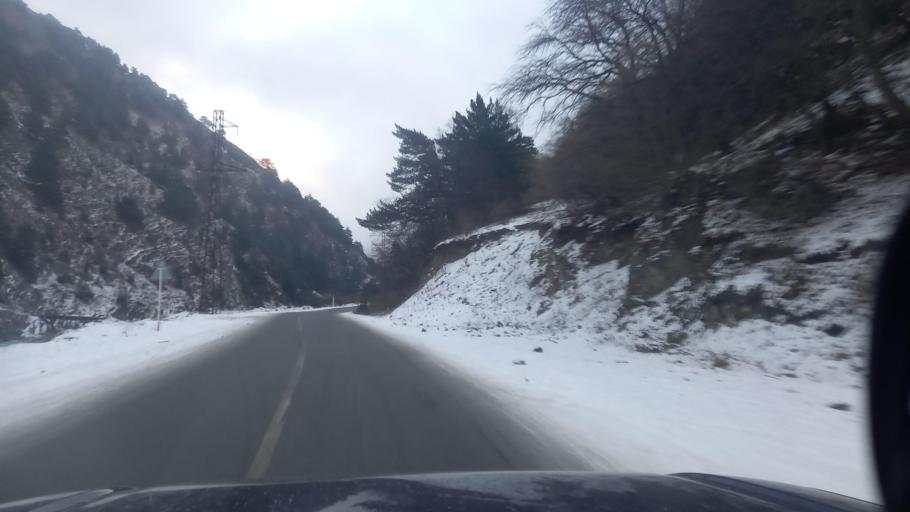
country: RU
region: Ingushetiya
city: Dzhayrakh
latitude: 42.7929
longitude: 44.7638
